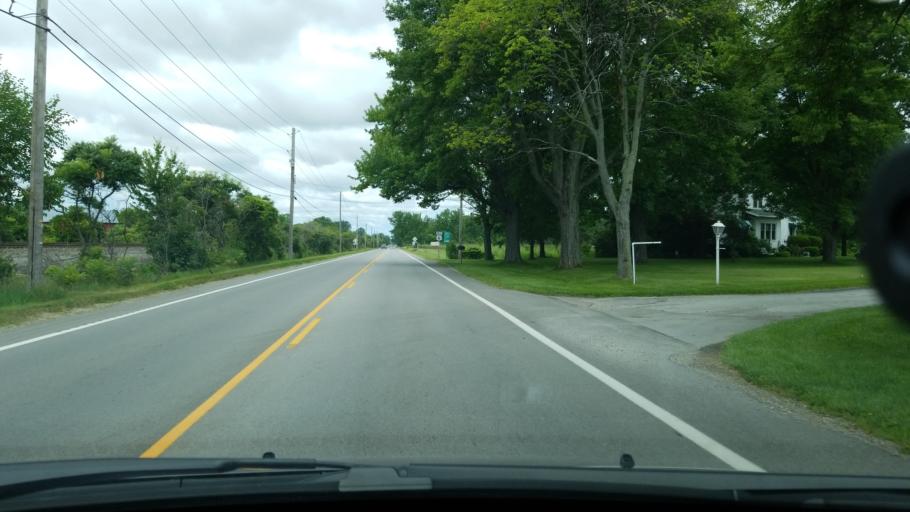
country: US
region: Ohio
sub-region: Erie County
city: Sandusky
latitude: 41.4206
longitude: -82.6339
